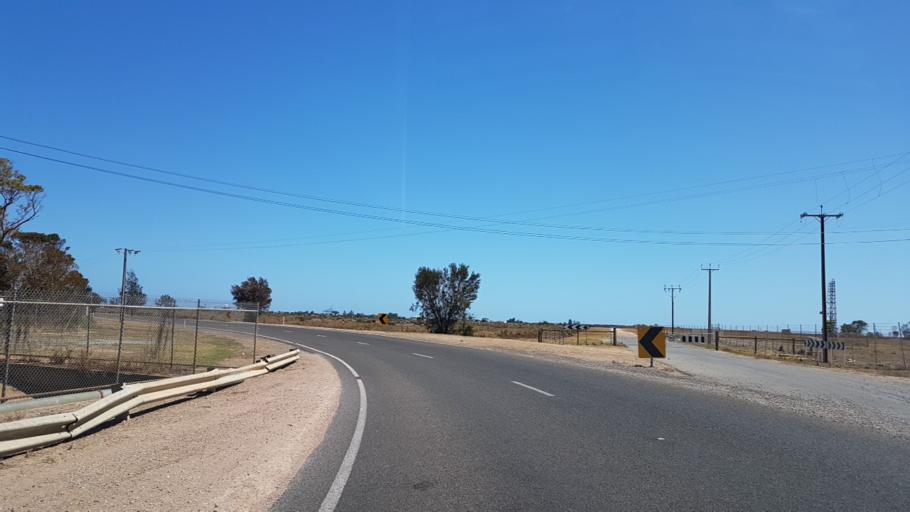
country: AU
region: South Australia
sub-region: Playford
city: Virginia
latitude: -34.7317
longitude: 138.5498
